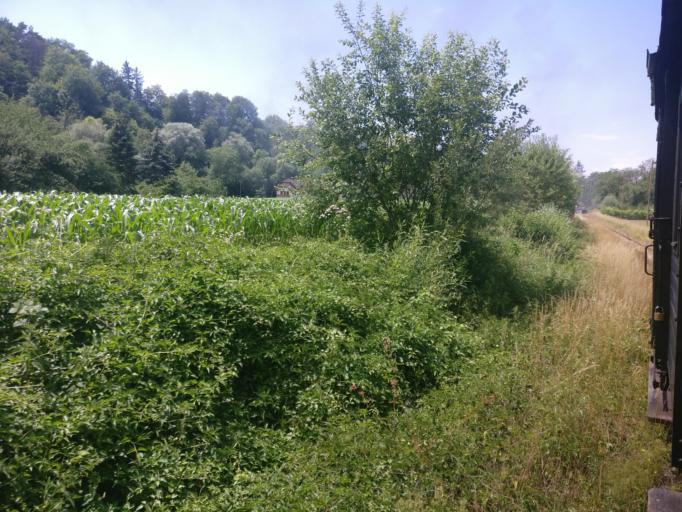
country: AT
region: Upper Austria
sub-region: Politischer Bezirk Steyr-Land
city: Garsten
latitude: 48.0400
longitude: 14.3952
